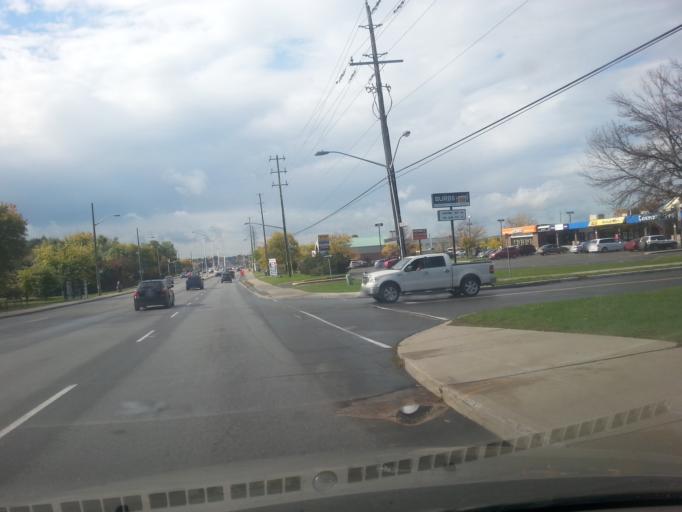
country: CA
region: Ontario
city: Bells Corners
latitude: 45.2959
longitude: -75.8921
